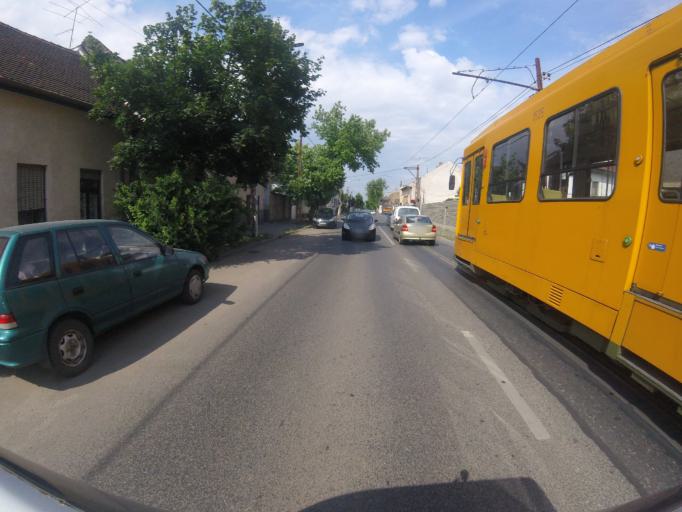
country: HU
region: Budapest
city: Budapest XX. keruelet
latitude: 47.4397
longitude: 19.1167
